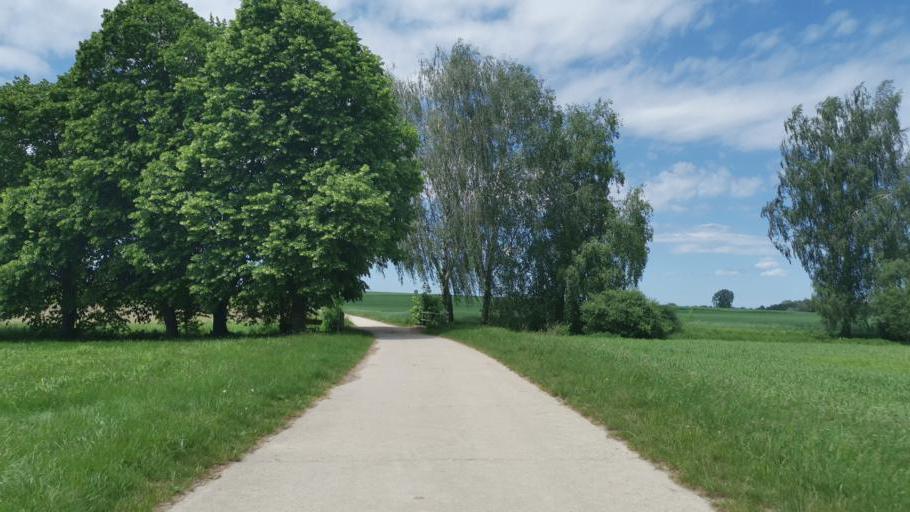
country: DE
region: Bavaria
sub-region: Swabia
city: Steindorf
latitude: 48.2392
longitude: 11.0139
